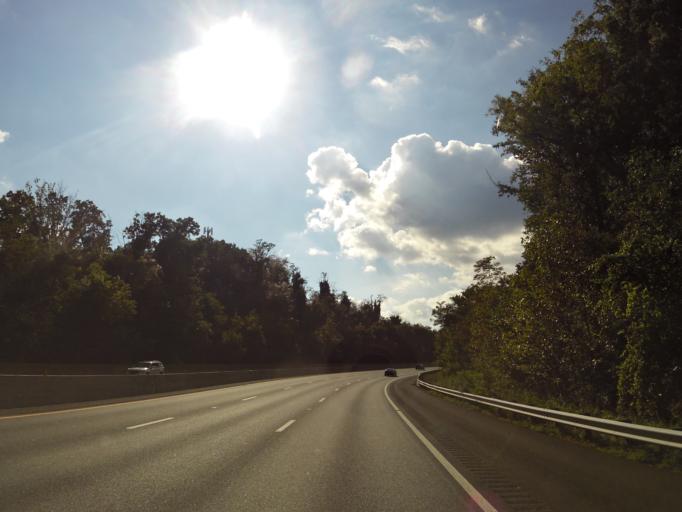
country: US
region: North Carolina
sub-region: Haywood County
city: Canton
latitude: 35.5401
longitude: -82.7907
